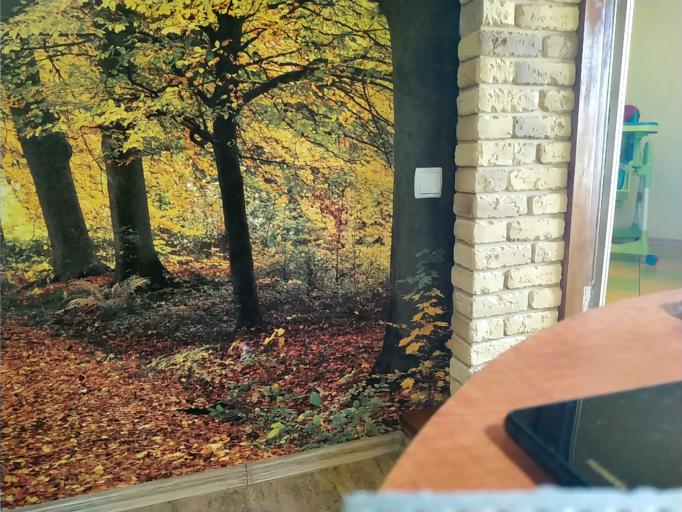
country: RU
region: Kaluga
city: Kondrovo
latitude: 54.8048
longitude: 35.9290
